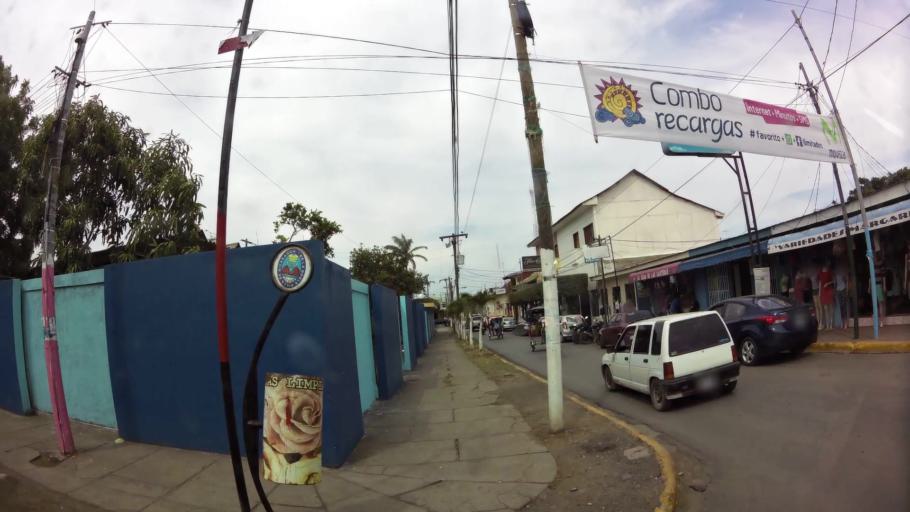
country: NI
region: Rivas
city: Rivas
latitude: 11.4384
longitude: -85.8314
